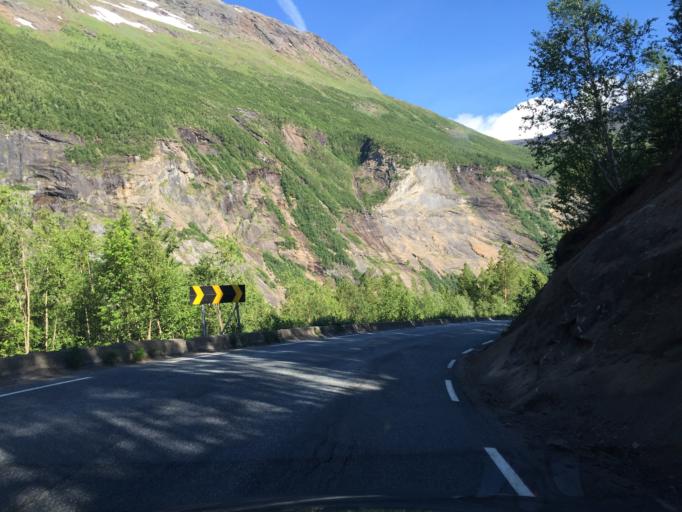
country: NO
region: Nordland
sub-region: Saltdal
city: Rognan
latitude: 66.8198
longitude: 15.4719
